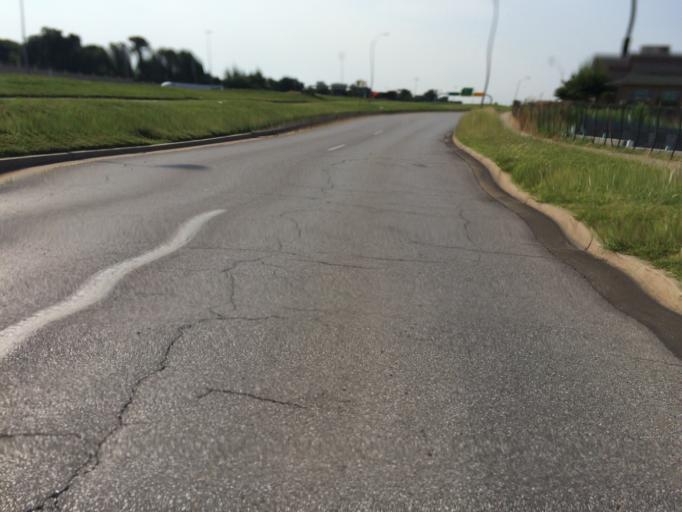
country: US
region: Oklahoma
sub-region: Cleveland County
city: Norman
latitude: 35.2163
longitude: -97.4866
